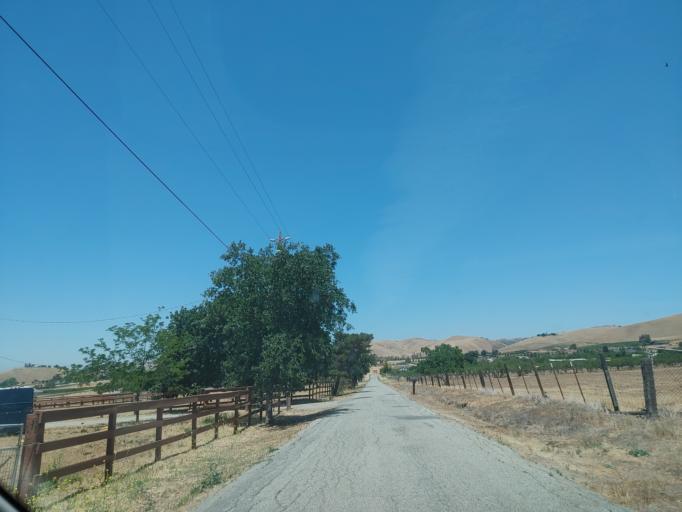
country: US
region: California
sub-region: San Benito County
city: Hollister
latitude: 36.9167
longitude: -121.3403
